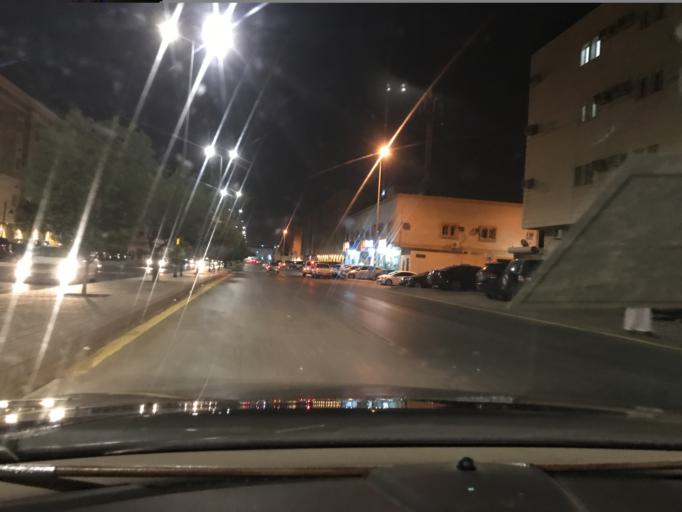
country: SA
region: Ar Riyad
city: Riyadh
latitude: 24.7400
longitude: 46.7708
